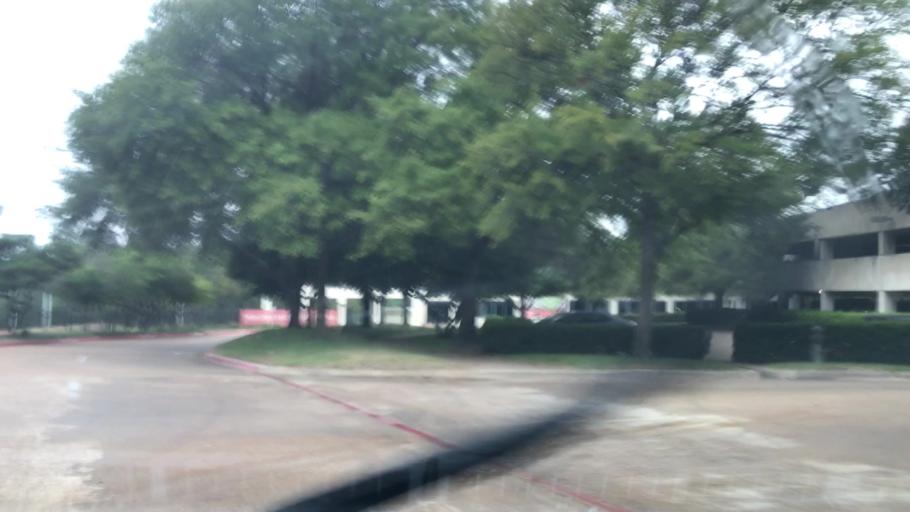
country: US
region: Texas
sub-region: Dallas County
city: Addison
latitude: 32.9486
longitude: -96.8055
